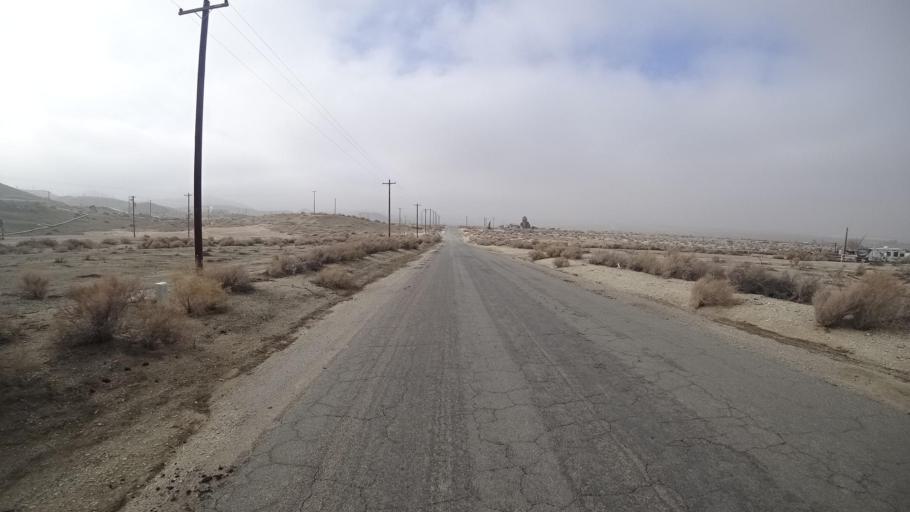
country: US
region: California
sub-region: Kern County
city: Maricopa
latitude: 35.0374
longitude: -119.3626
